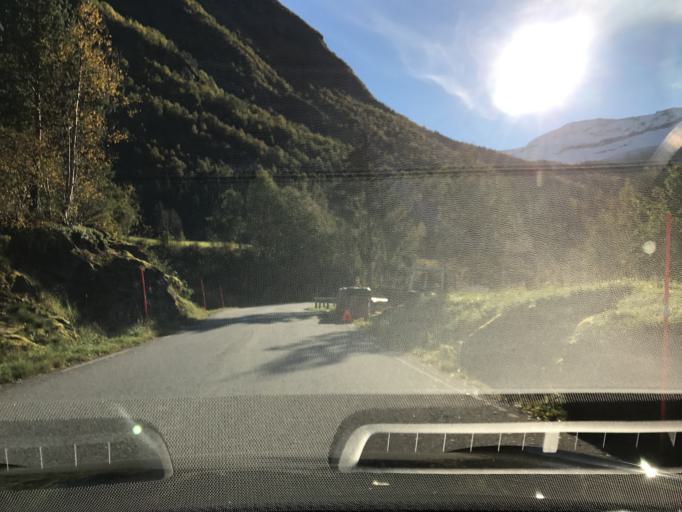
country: NO
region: More og Romsdal
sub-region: Norddal
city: Valldal
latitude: 62.3370
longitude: 7.3893
